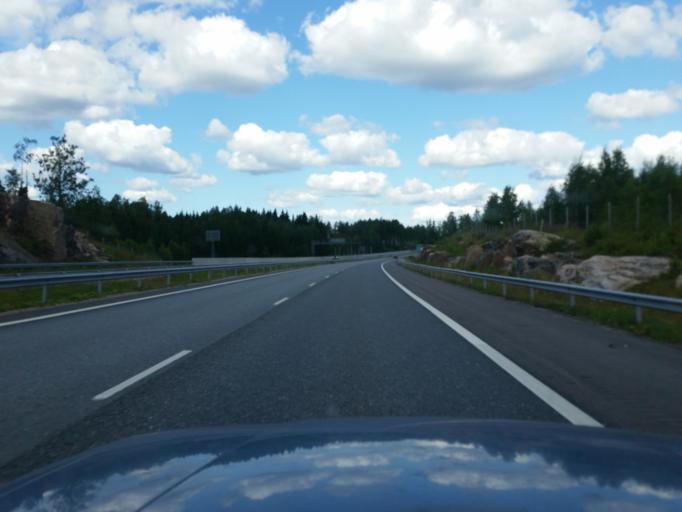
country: FI
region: Uusimaa
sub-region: Helsinki
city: Sammatti
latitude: 60.3496
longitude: 23.8985
